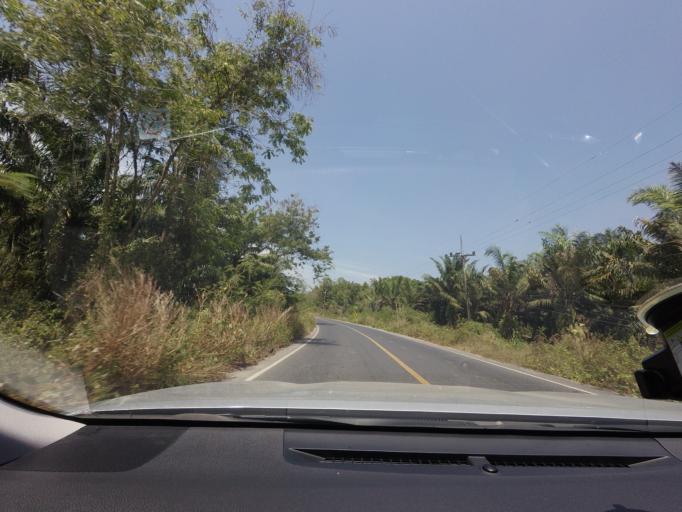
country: TH
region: Surat Thani
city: Tha Chang
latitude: 9.2643
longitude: 99.1624
